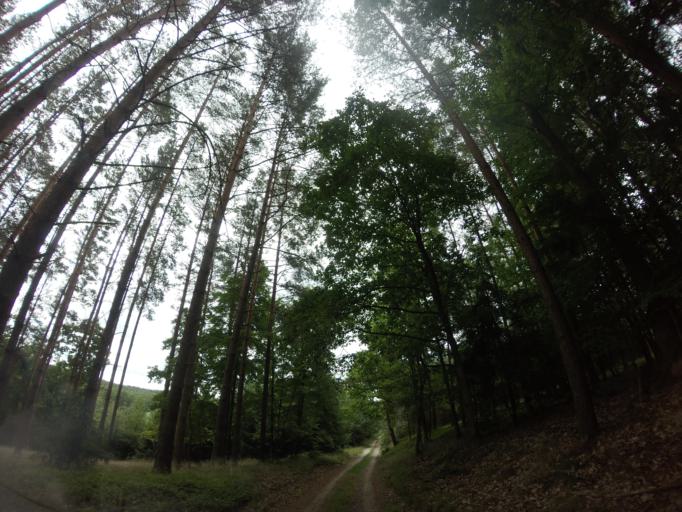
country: PL
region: West Pomeranian Voivodeship
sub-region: Powiat choszczenski
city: Bierzwnik
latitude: 52.9699
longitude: 15.6154
